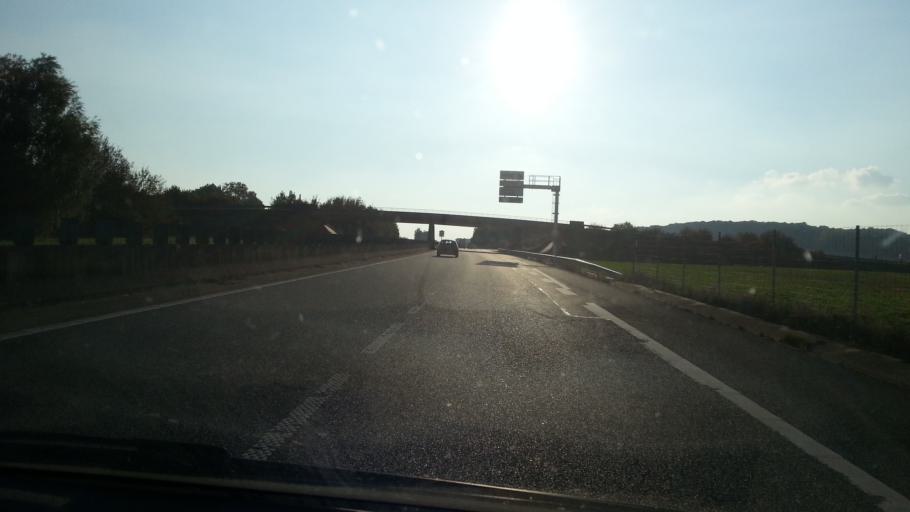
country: FR
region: Picardie
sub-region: Departement de l'Oise
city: Longueil-Annel
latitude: 49.4852
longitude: 2.8660
